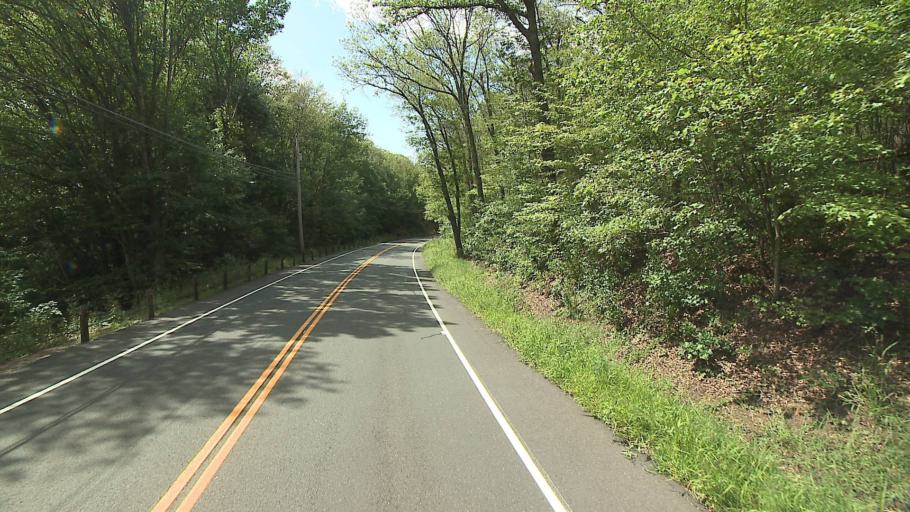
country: US
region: Connecticut
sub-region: Tolland County
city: Ellington
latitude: 41.9148
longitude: -72.4301
